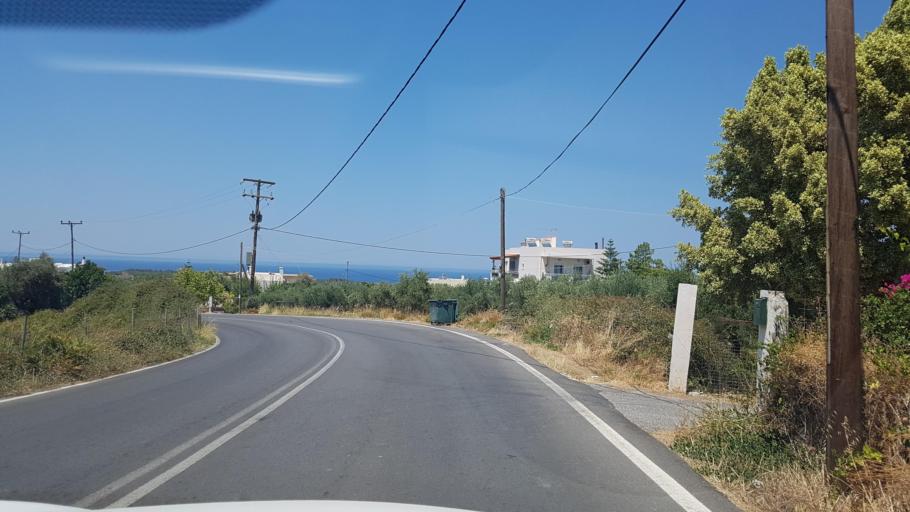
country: GR
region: Crete
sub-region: Nomos Rethymnis
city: Agia Foteini
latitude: 35.3528
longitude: 24.5891
